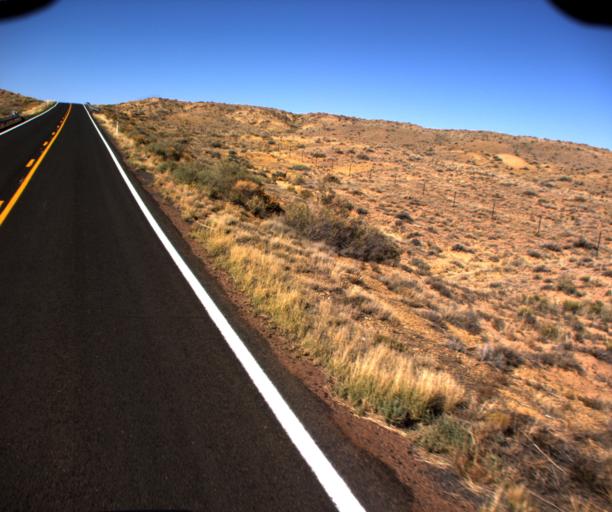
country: US
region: Arizona
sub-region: Coconino County
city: Tuba City
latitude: 35.9568
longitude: -110.9316
